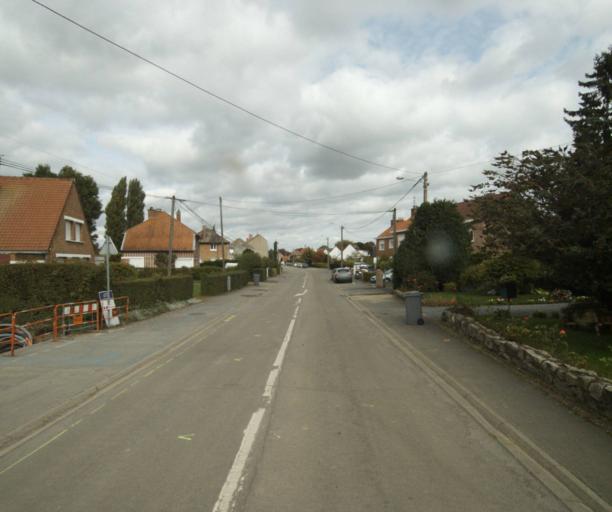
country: FR
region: Nord-Pas-de-Calais
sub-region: Departement du Nord
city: Erquinghem-Lys
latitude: 50.6726
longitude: 2.8457
